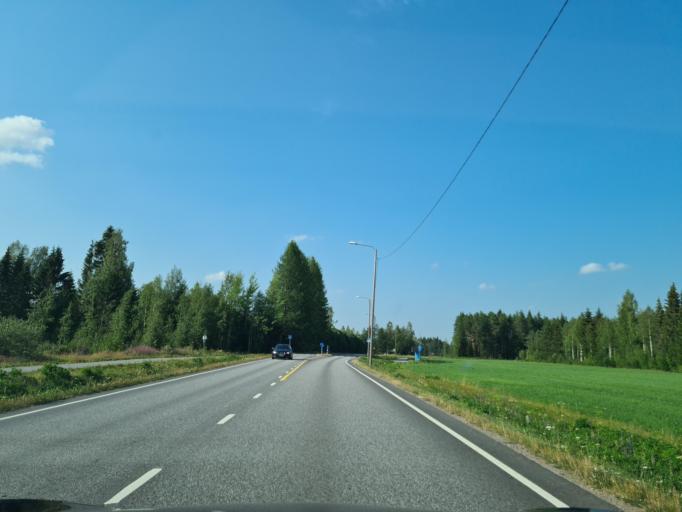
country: FI
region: Satakunta
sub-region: Pohjois-Satakunta
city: Karvia
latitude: 62.0878
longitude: 22.5270
